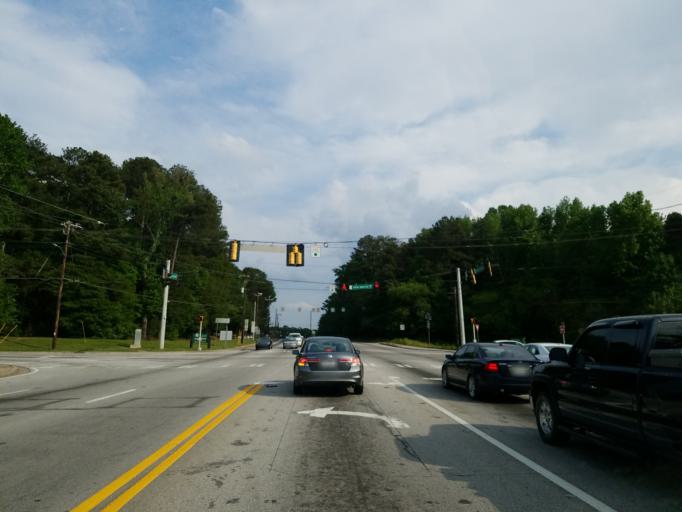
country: US
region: Georgia
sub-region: Cobb County
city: Vinings
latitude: 33.7903
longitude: -84.4965
